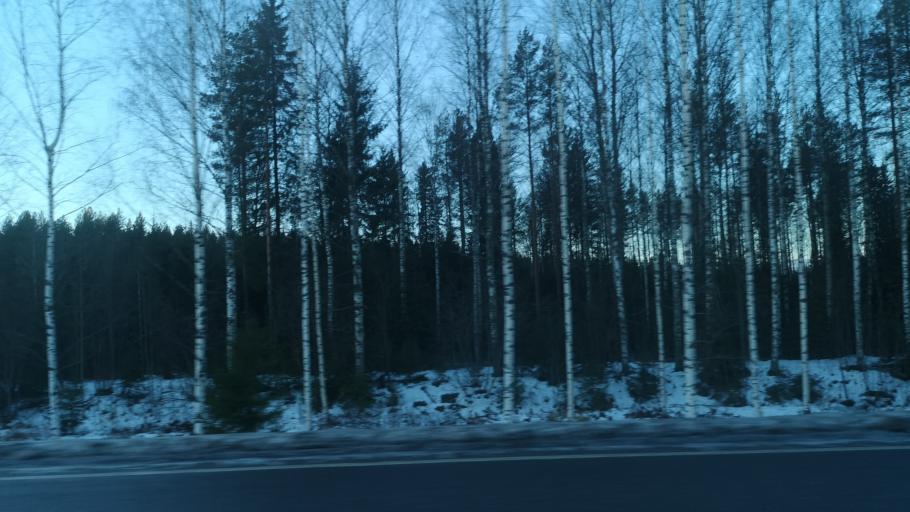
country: FI
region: Southern Savonia
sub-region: Pieksaemaeki
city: Juva
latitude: 61.9208
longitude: 28.0397
